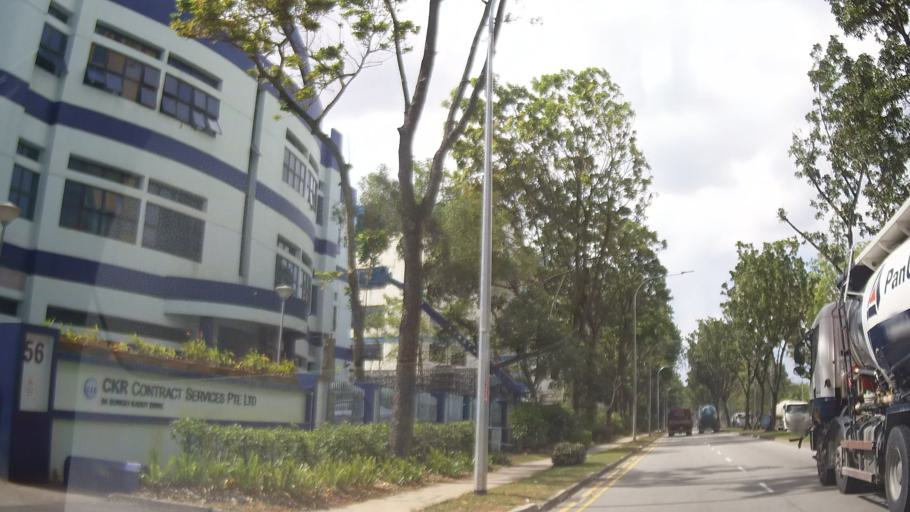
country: MY
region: Johor
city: Johor Bahru
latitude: 1.4125
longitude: 103.7454
